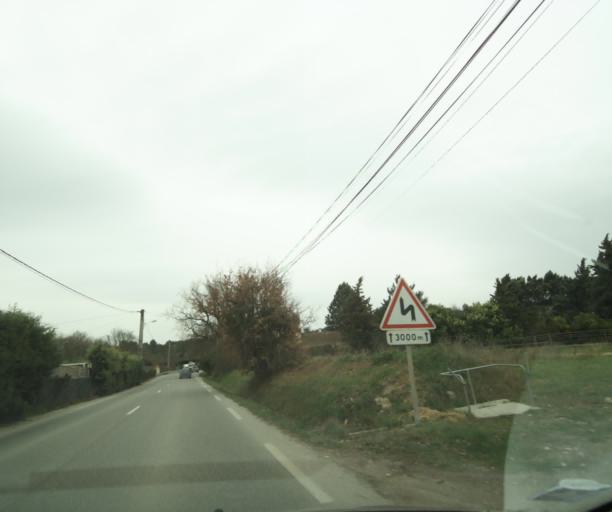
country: FR
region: Provence-Alpes-Cote d'Azur
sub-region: Departement des Bouches-du-Rhone
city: Fuveau
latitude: 43.4723
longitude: 5.5442
